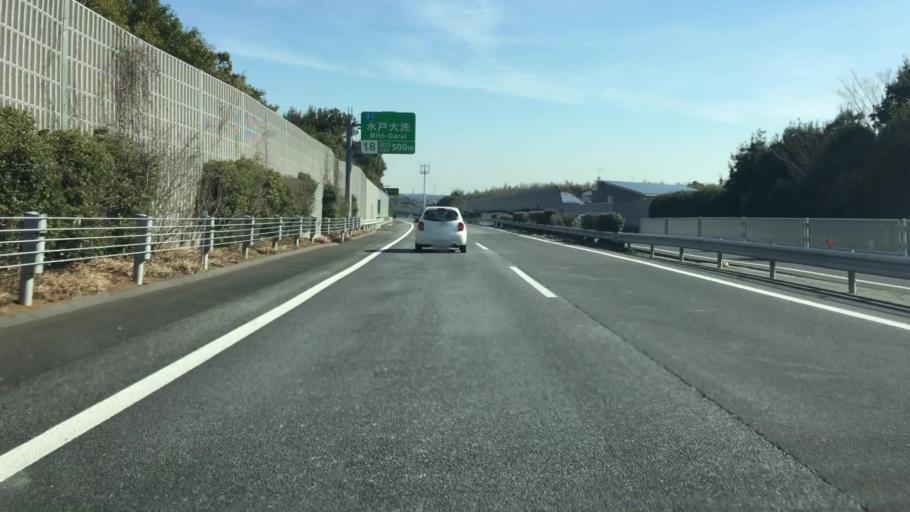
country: JP
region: Ibaraki
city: Katsuta
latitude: 36.3348
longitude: 140.5377
